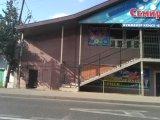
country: KZ
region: Almaty Qalasy
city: Almaty
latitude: 43.2580
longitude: 76.8811
